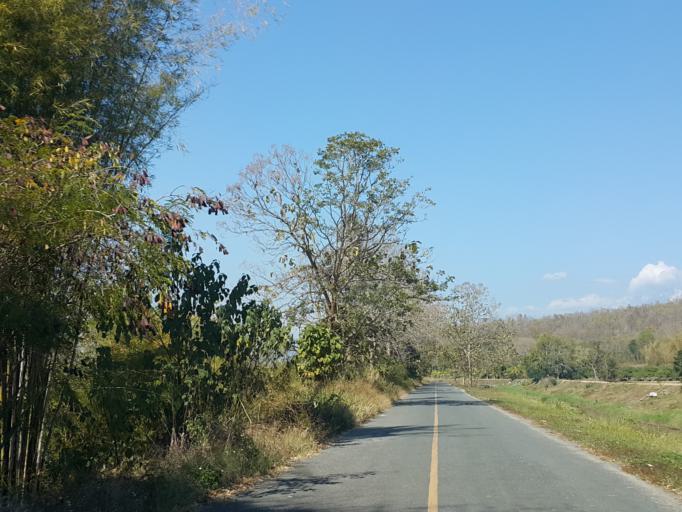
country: TH
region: Chiang Mai
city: Mae Taeng
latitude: 19.0736
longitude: 98.9576
